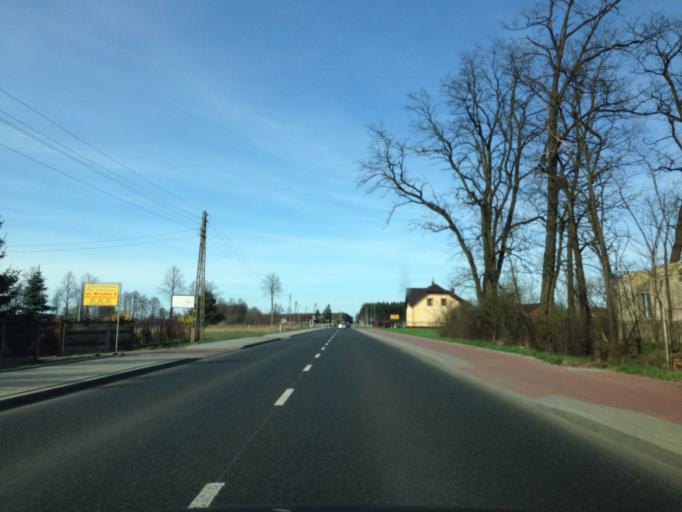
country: PL
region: Lodz Voivodeship
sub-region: Powiat poddebicki
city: Wartkowice
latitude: 51.9455
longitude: 18.9989
